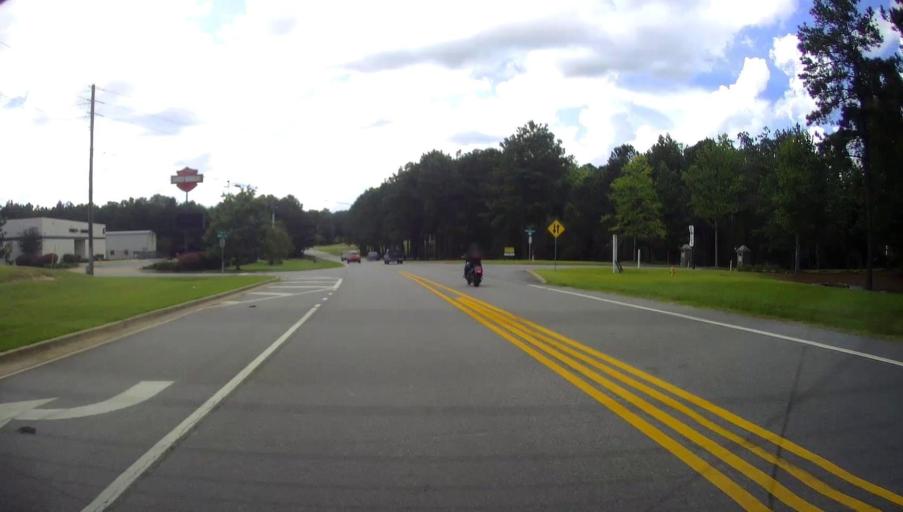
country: US
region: Alabama
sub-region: Russell County
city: Phenix City
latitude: 32.5641
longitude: -84.9412
